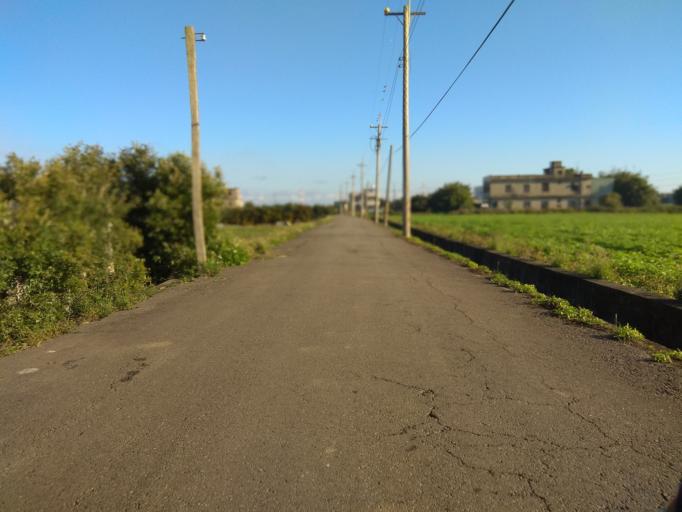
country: TW
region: Taiwan
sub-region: Hsinchu
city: Zhubei
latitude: 24.9926
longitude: 121.0529
